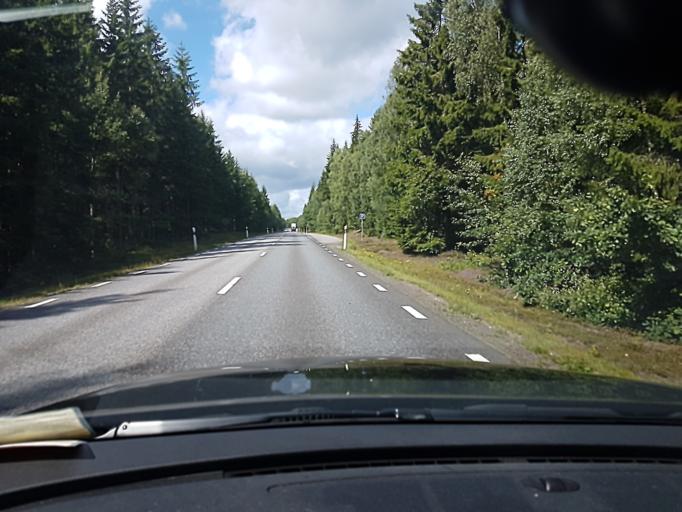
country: SE
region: Kalmar
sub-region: Emmaboda Kommun
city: Emmaboda
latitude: 56.7328
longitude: 15.4561
